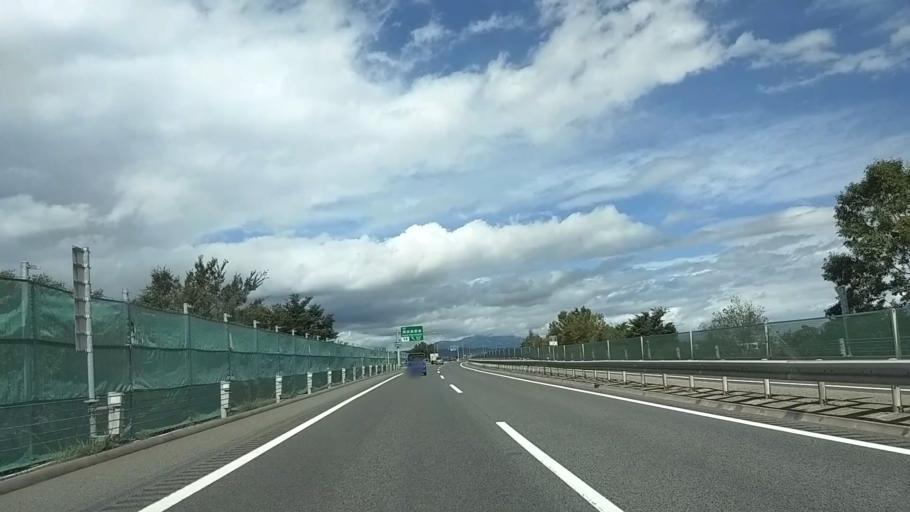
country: JP
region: Nagano
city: Suzaka
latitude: 36.6292
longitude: 138.2734
